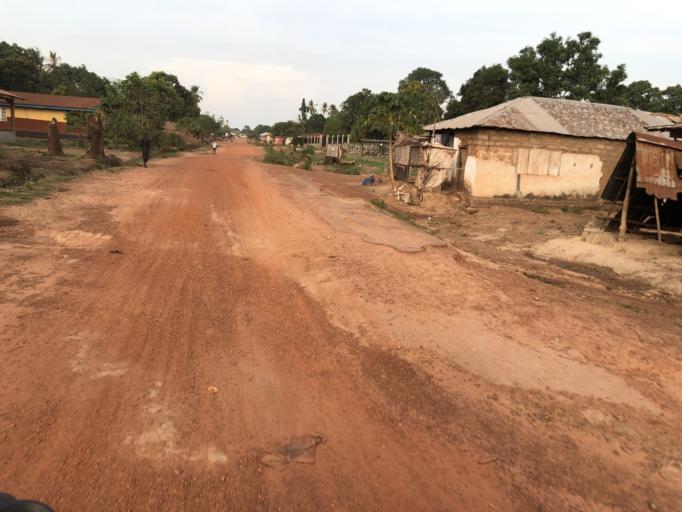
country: SL
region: Northern Province
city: Yonibana
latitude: 8.4679
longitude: -12.2062
